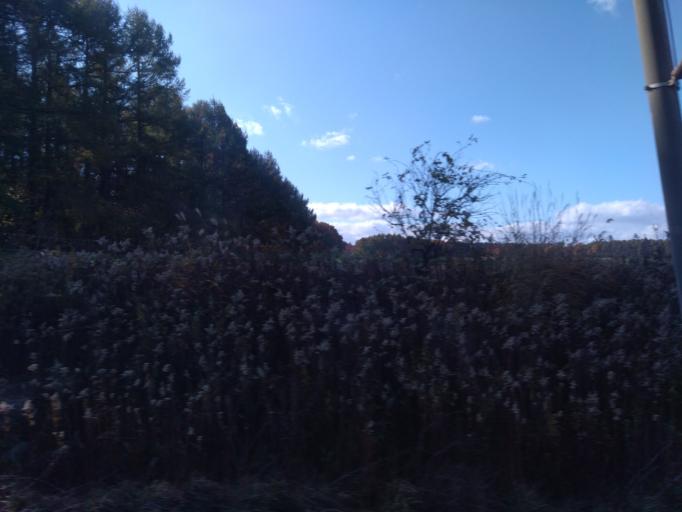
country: JP
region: Hokkaido
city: Kitahiroshima
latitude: 42.9506
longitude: 141.5709
